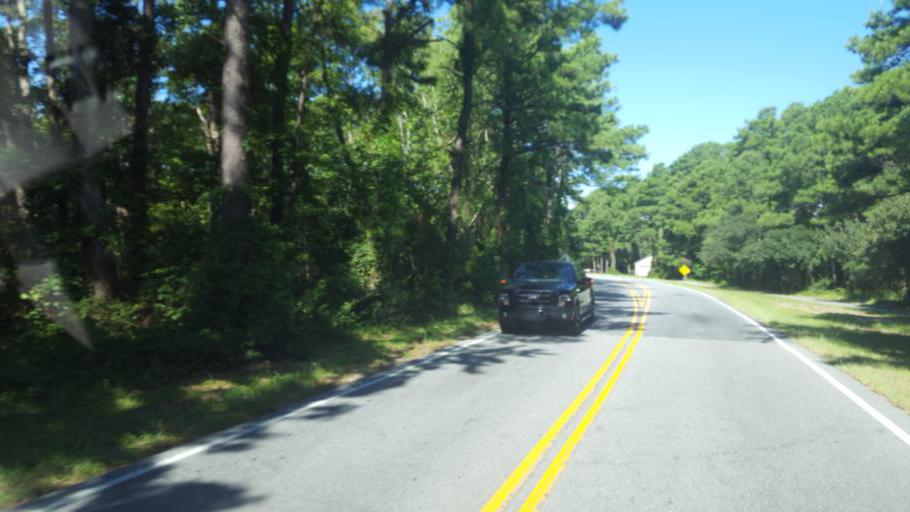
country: US
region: North Carolina
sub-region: Dare County
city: Kill Devil Hills
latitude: 36.0132
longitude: -75.6754
